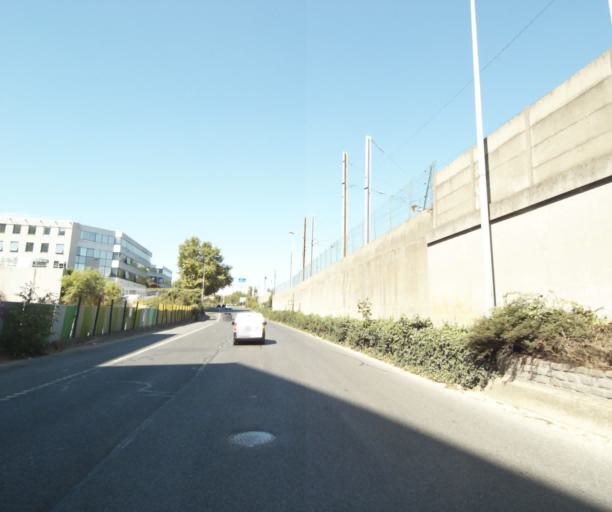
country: FR
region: Ile-de-France
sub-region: Paris
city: Saint-Ouen
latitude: 48.9196
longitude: 2.3468
